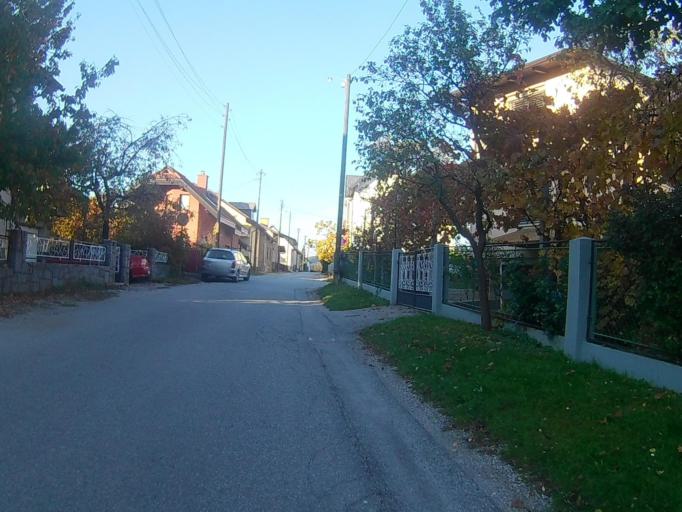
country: SI
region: Maribor
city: Kamnica
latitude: 46.5604
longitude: 15.6143
